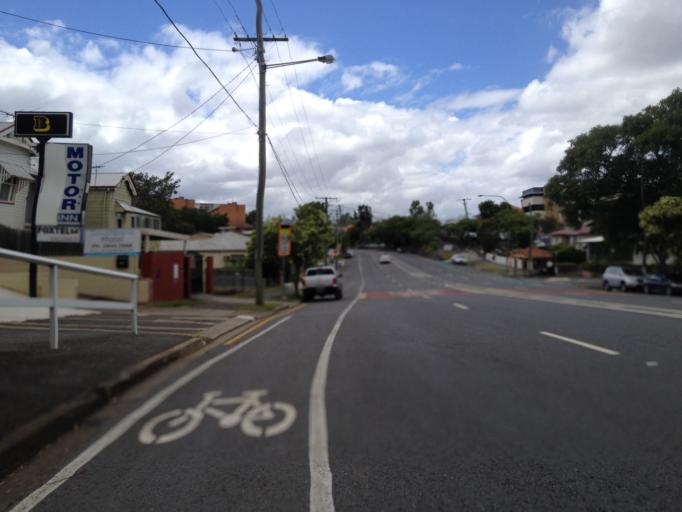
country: AU
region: Queensland
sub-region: Brisbane
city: South Brisbane
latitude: -27.4927
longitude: 153.0213
